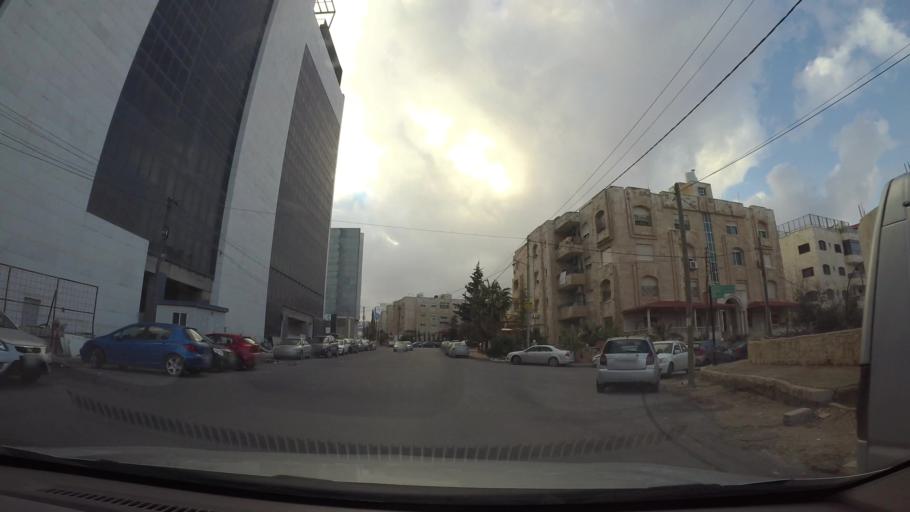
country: JO
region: Amman
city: Wadi as Sir
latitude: 31.9765
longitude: 35.8604
